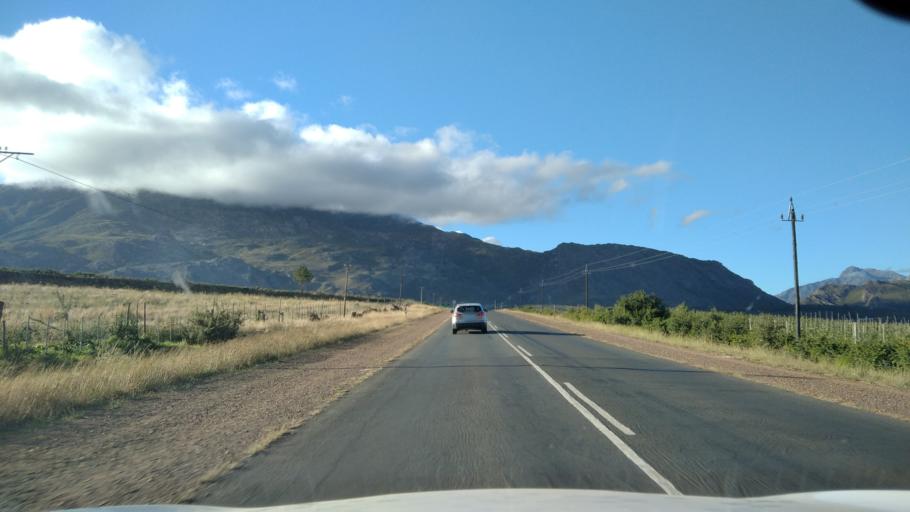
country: ZA
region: Western Cape
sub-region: Overberg District Municipality
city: Caledon
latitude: -34.0027
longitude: 19.2896
